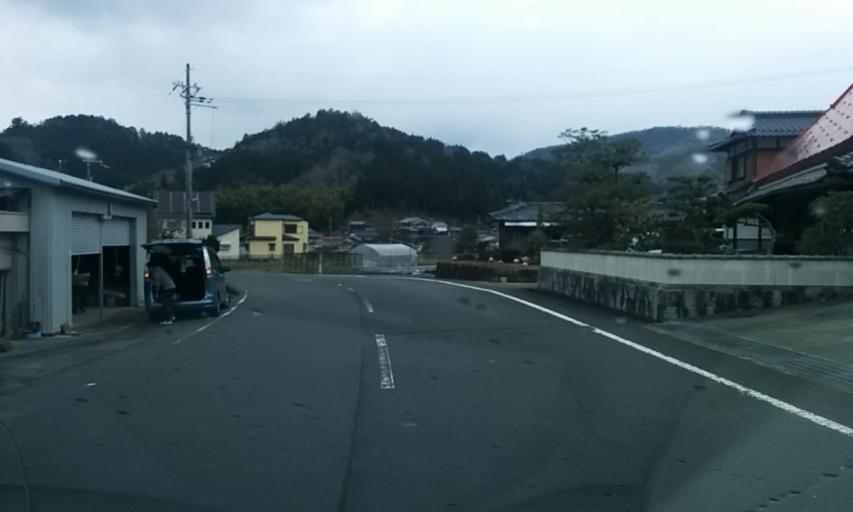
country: JP
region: Hyogo
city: Sasayama
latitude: 35.1253
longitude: 135.4144
